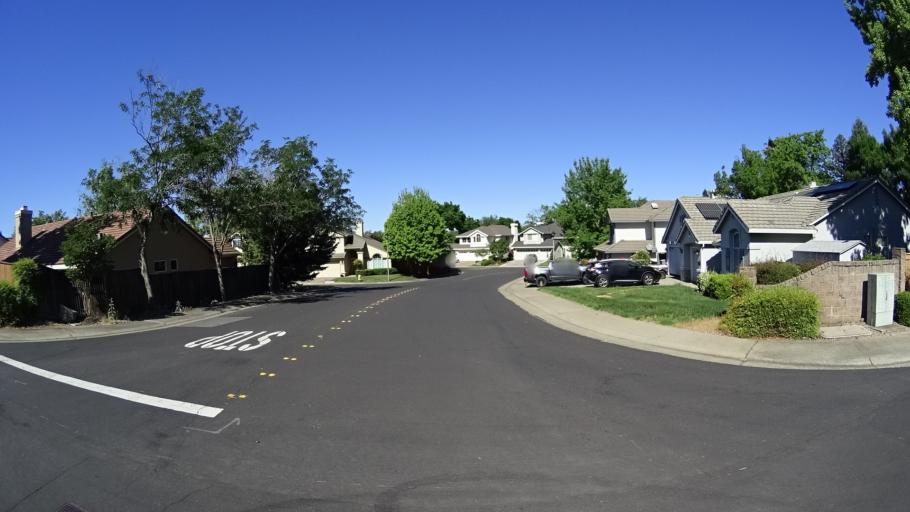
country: US
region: California
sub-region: Placer County
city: Rocklin
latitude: 38.7875
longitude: -121.2636
